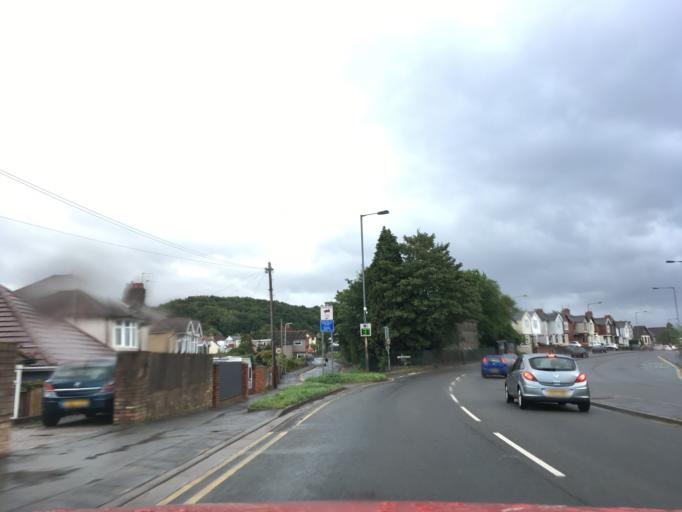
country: GB
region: Wales
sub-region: Newport
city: Newport
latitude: 51.6126
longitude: -3.0050
